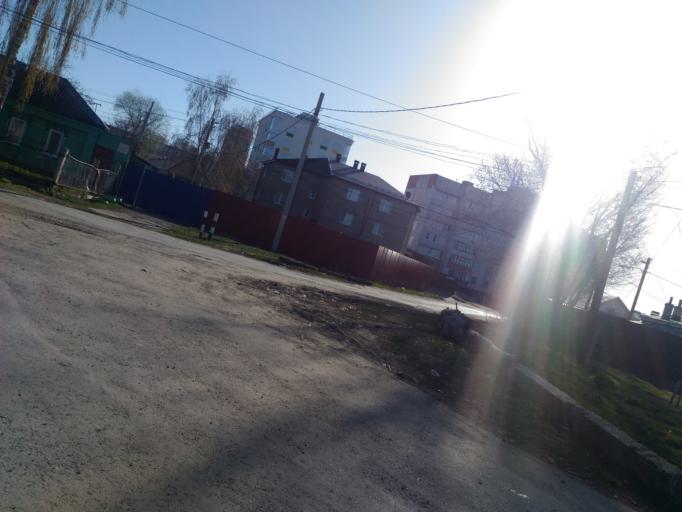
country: RU
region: Ulyanovsk
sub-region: Ulyanovskiy Rayon
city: Ulyanovsk
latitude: 54.3407
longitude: 48.3877
